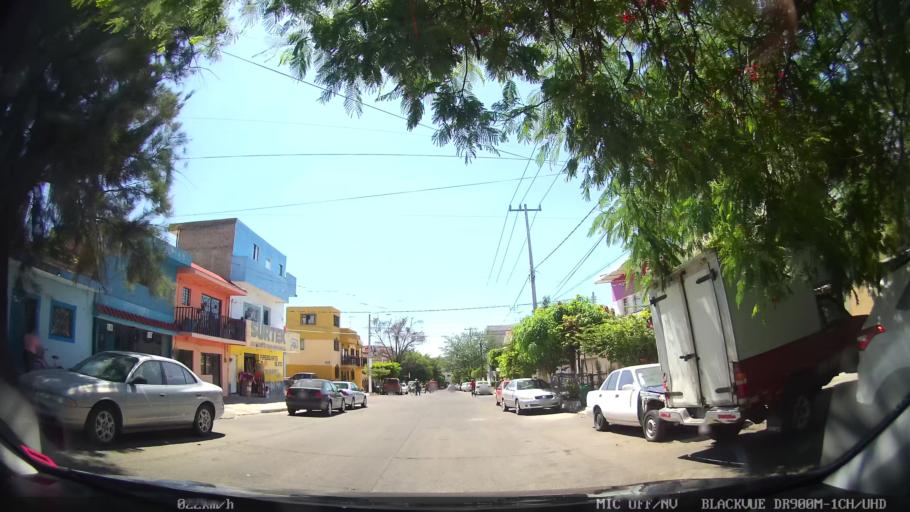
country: MX
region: Jalisco
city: Tlaquepaque
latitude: 20.6868
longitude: -103.2932
